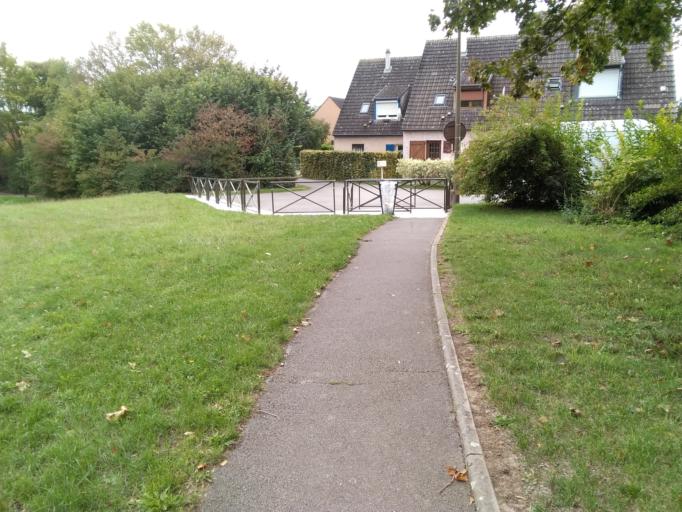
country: FR
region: Picardie
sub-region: Departement de la Somme
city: Amiens
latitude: 49.9189
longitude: 2.2960
